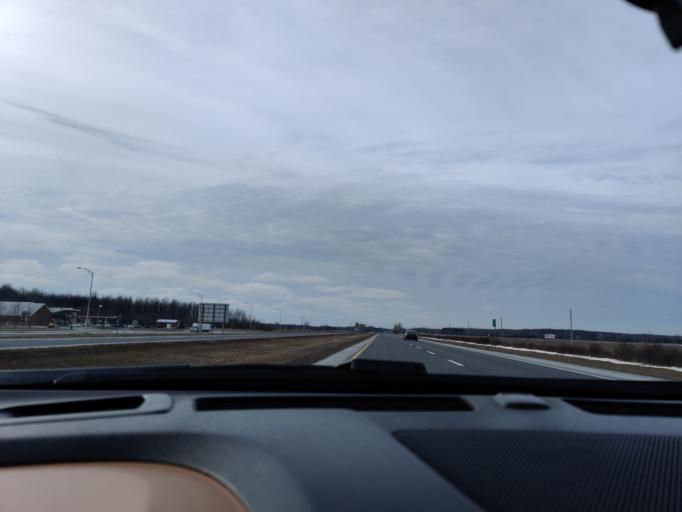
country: CA
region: Quebec
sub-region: Monteregie
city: Les Coteaux
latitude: 45.2147
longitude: -74.3375
